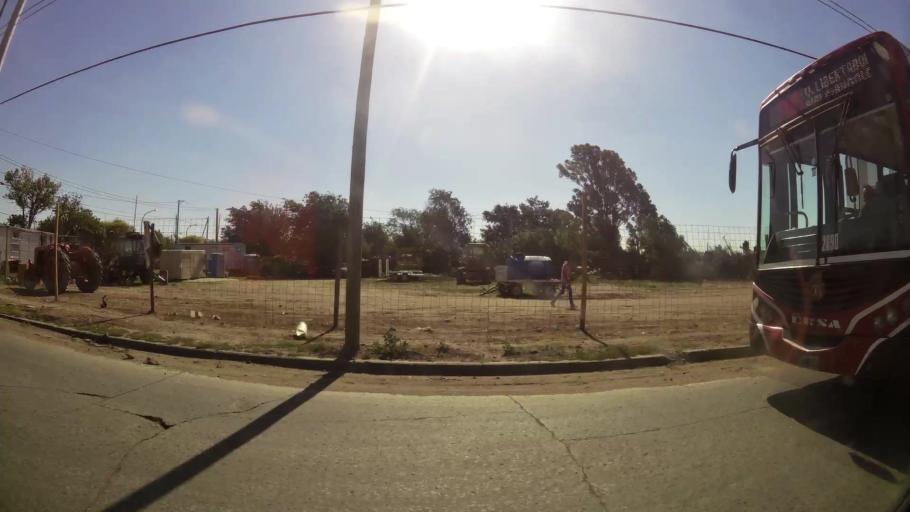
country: AR
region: Cordoba
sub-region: Departamento de Capital
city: Cordoba
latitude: -31.3617
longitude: -64.1839
